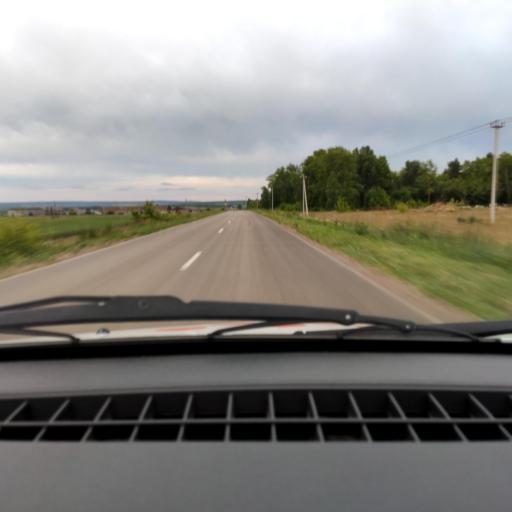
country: RU
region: Bashkortostan
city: Avdon
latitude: 54.5180
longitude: 55.7725
